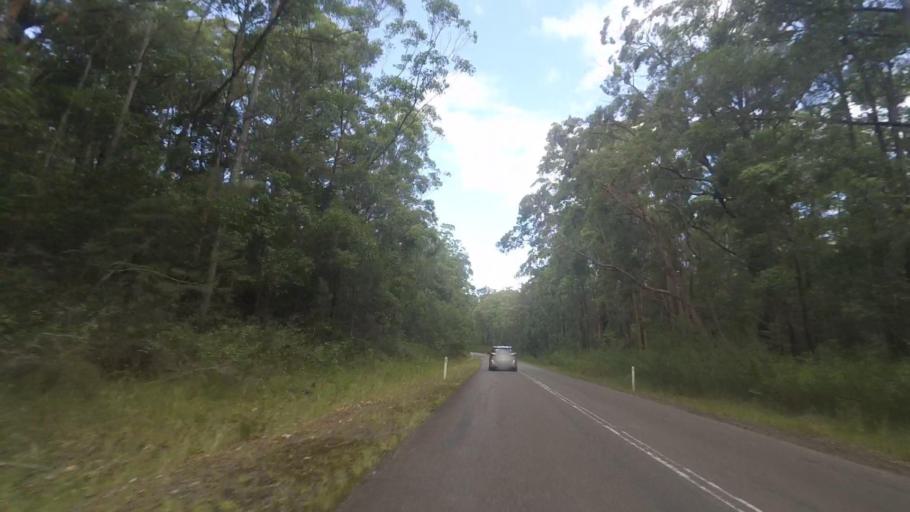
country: AU
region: New South Wales
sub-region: Great Lakes
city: Bulahdelah
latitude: -32.3994
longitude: 152.2558
